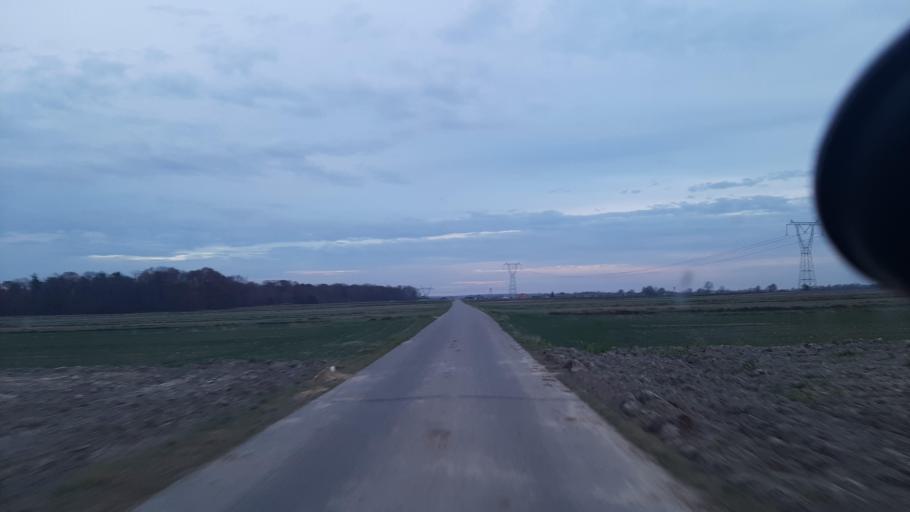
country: PL
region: Lublin Voivodeship
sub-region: Powiat lubelski
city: Garbow
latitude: 51.3747
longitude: 22.3743
